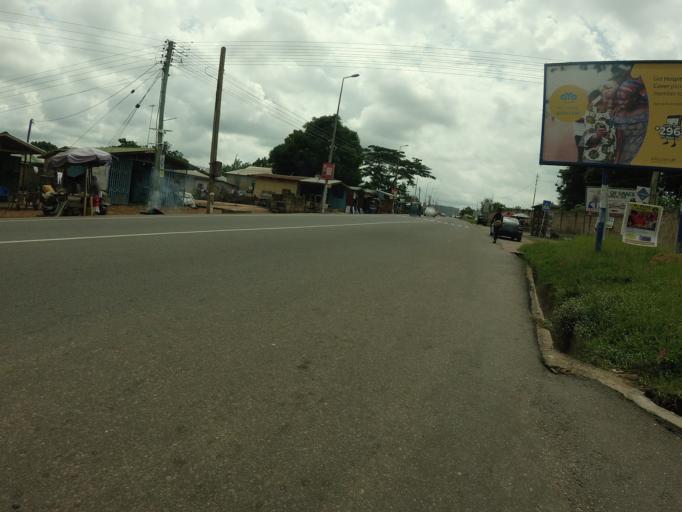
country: GH
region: Volta
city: Ho
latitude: 6.5990
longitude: 0.4728
